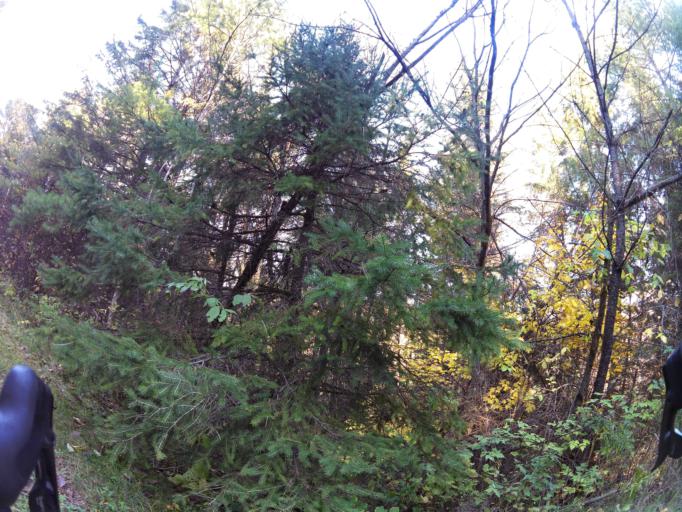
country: CA
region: Quebec
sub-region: Outaouais
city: Wakefield
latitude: 45.8584
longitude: -75.9944
